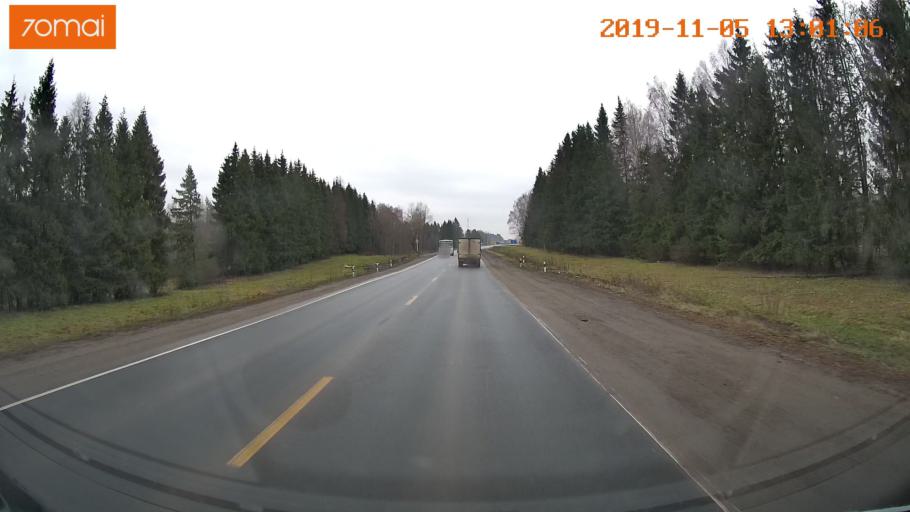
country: RU
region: Ivanovo
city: Kokhma
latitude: 56.9105
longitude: 41.1570
